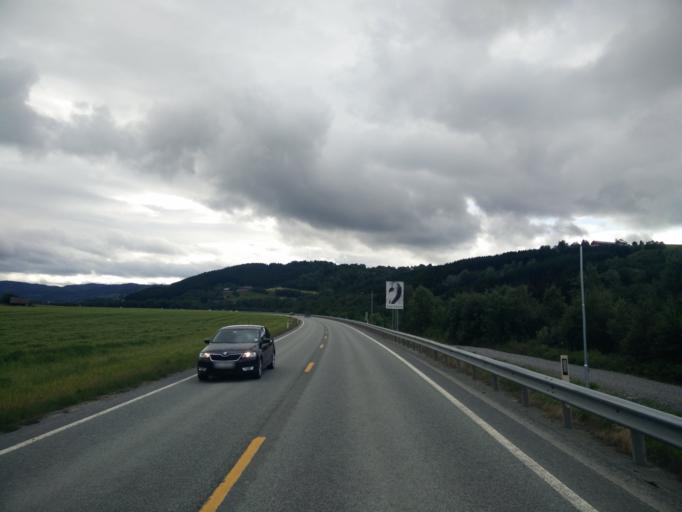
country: NO
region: Sor-Trondelag
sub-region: Orkdal
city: Orkanger
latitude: 63.2768
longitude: 9.8139
